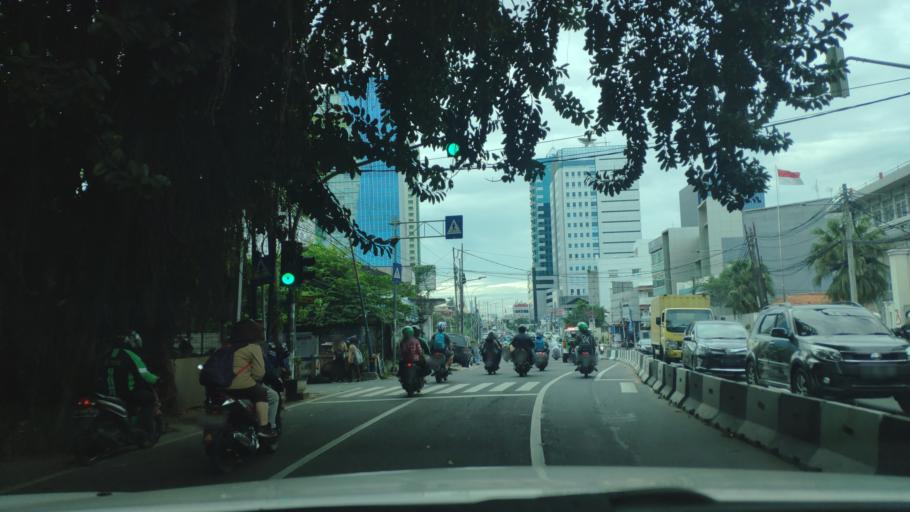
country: ID
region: Jakarta Raya
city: Jakarta
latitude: -6.1894
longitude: 106.8012
